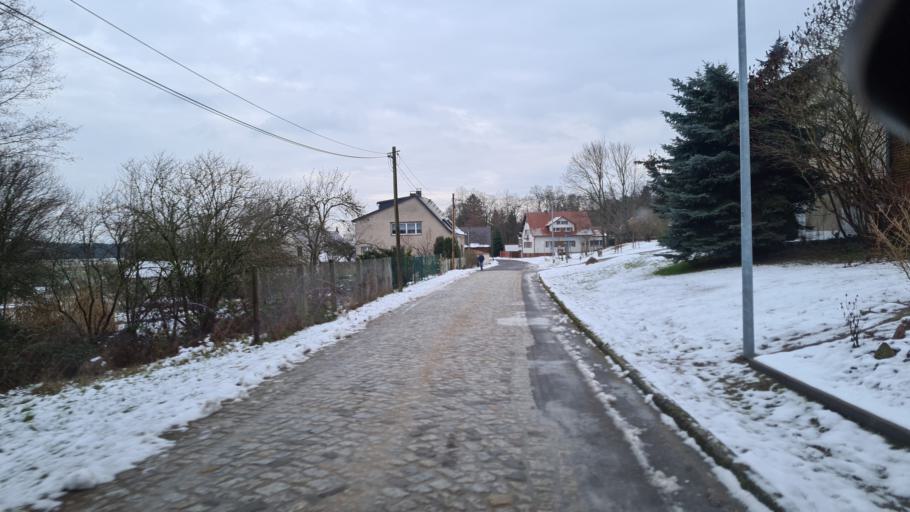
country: DE
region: Brandenburg
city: Schenkendobern
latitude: 51.9084
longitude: 14.5774
